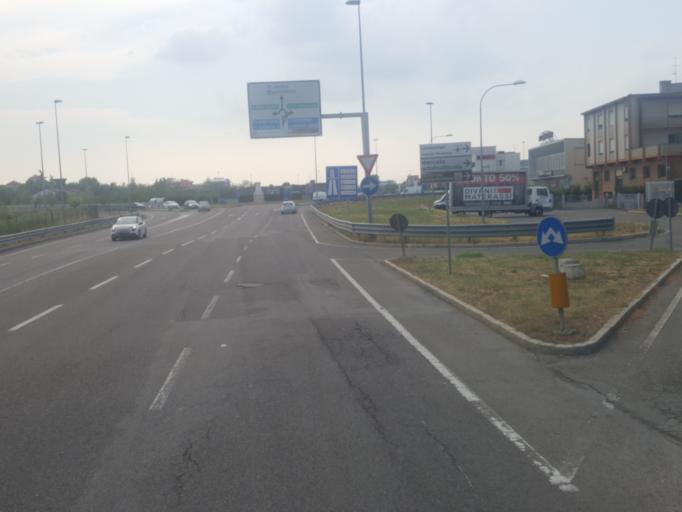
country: IT
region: Emilia-Romagna
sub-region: Provincia di Modena
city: San Damaso
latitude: 44.6325
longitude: 10.9592
